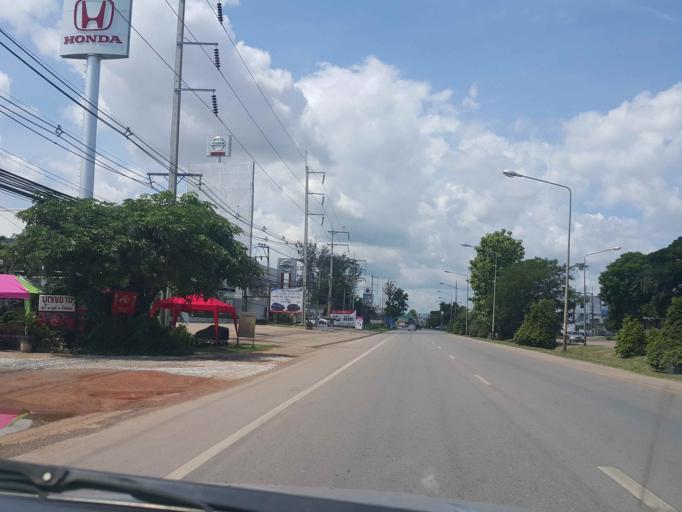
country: TH
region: Phayao
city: Phayao
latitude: 19.1491
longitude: 99.9124
